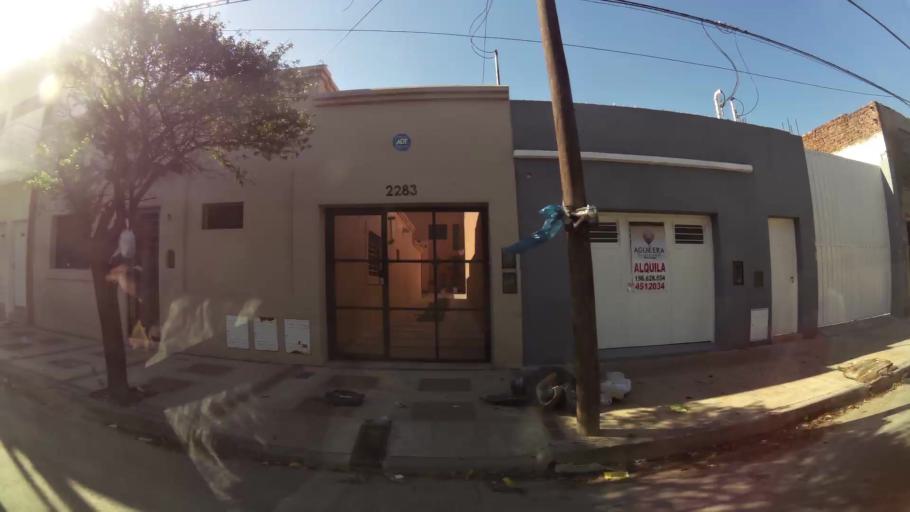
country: AR
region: Cordoba
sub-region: Departamento de Capital
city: Cordoba
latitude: -31.3993
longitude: -64.1569
